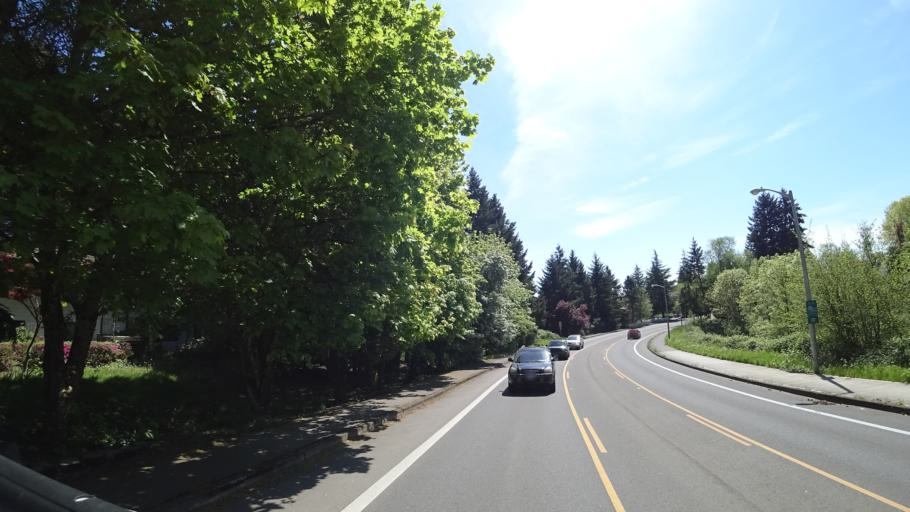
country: US
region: Oregon
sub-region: Washington County
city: Hillsboro
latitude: 45.5101
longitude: -122.9496
